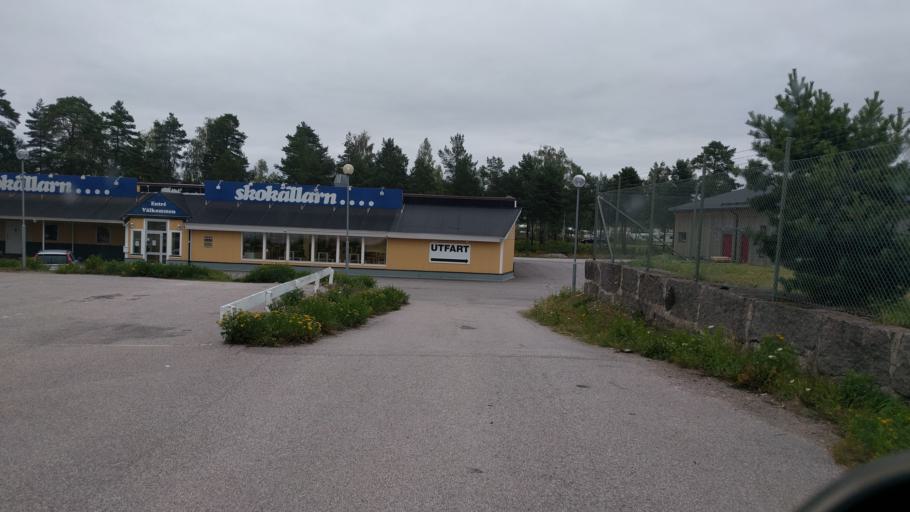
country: SE
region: Kalmar
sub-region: Vasterviks Kommun
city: Vaestervik
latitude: 57.7628
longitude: 16.6021
